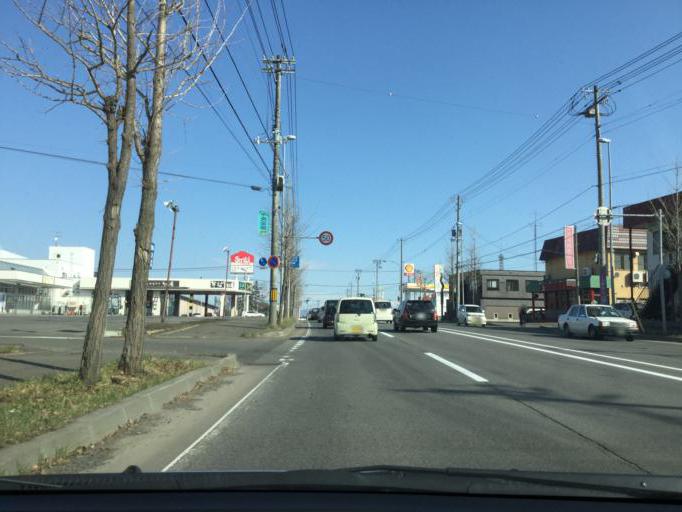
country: JP
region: Hokkaido
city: Iwamizawa
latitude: 43.2092
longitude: 141.7853
